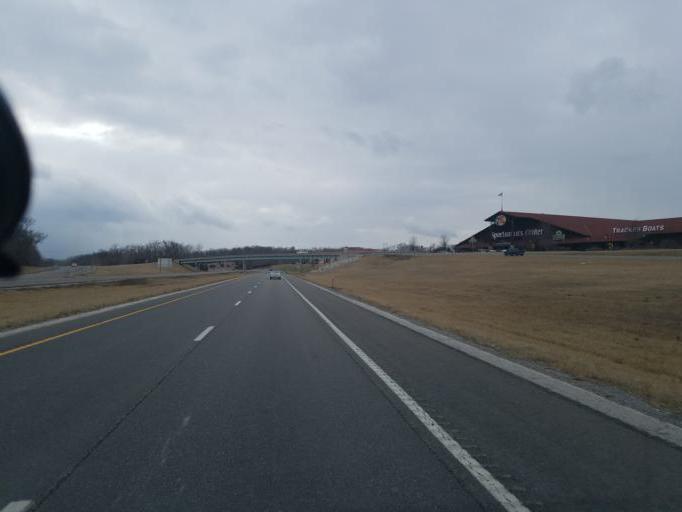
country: US
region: Missouri
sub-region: Boone County
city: Columbia
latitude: 38.9720
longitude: -92.2890
